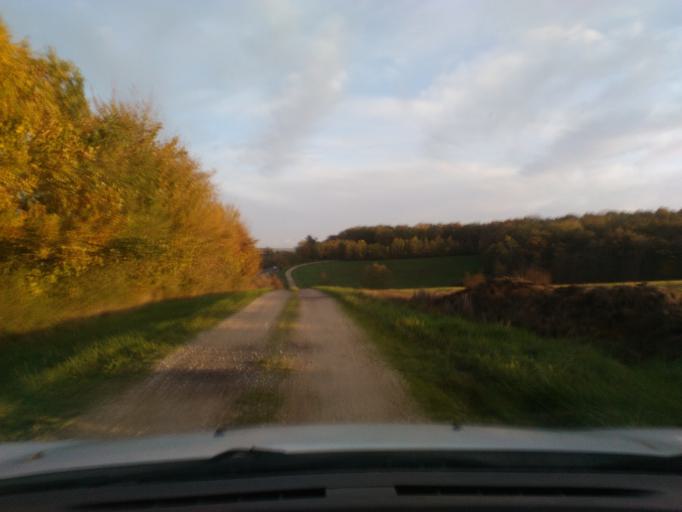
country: FR
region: Lorraine
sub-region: Departement des Vosges
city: Mirecourt
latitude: 48.2522
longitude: 6.1759
